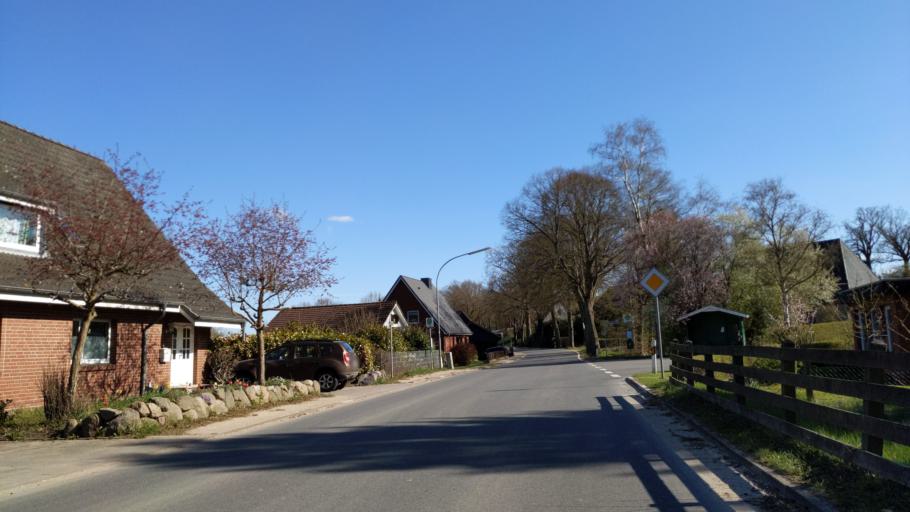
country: DE
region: Schleswig-Holstein
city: Eutin
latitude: 54.0912
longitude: 10.6172
